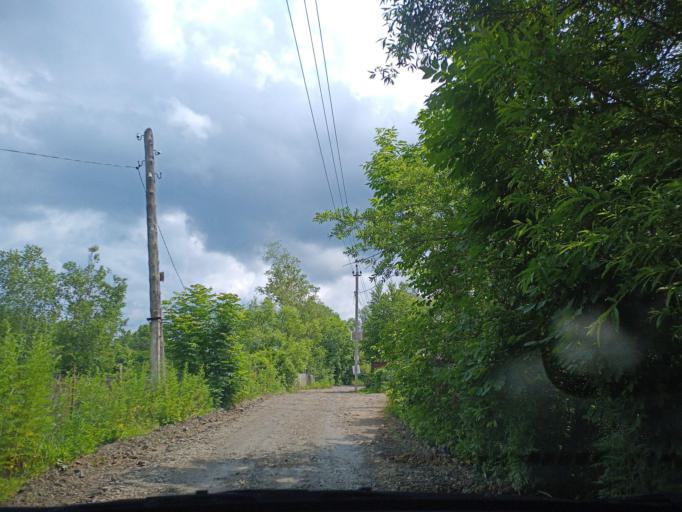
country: RU
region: Khabarovsk Krai
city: Korfovskiy
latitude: 48.3184
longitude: 135.1052
